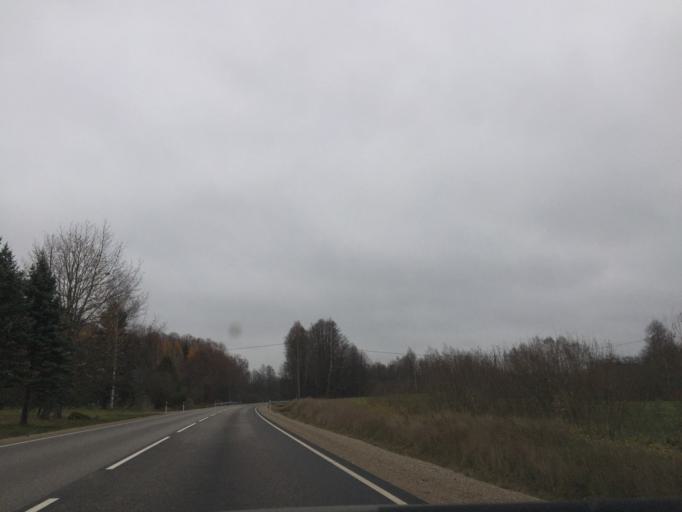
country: LV
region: Pargaujas
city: Stalbe
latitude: 57.5137
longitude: 25.0074
